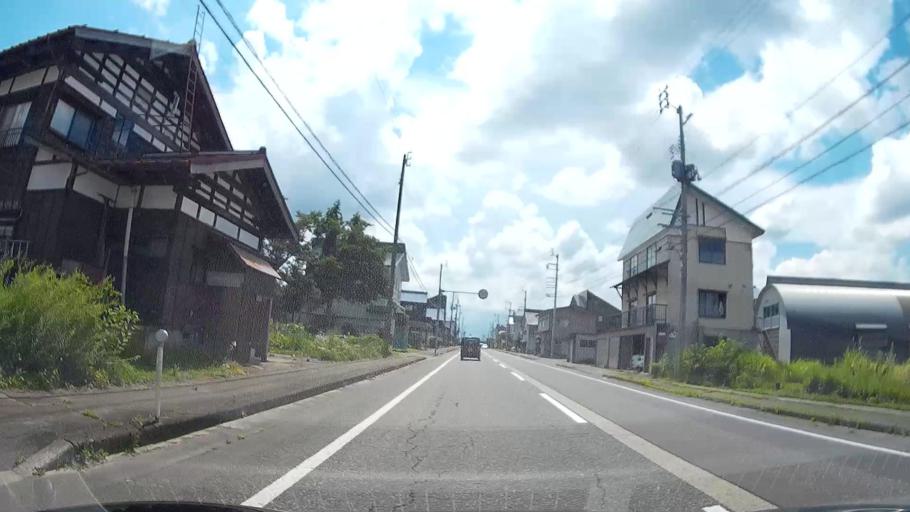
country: JP
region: Niigata
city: Tokamachi
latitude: 37.0579
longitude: 138.7037
